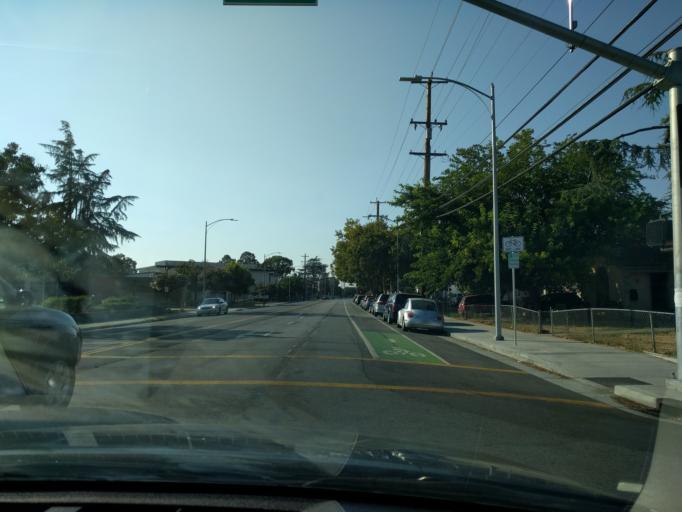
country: US
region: California
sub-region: Santa Clara County
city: Alum Rock
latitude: 37.3673
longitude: -121.8293
